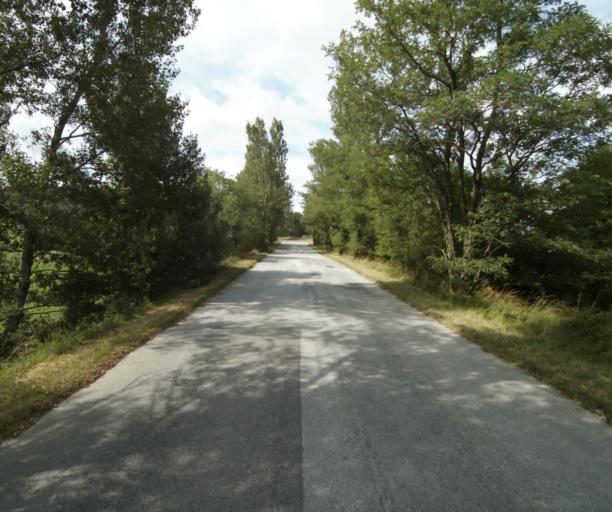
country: FR
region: Midi-Pyrenees
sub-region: Departement du Tarn
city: Dourgne
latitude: 43.4671
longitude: 2.1049
